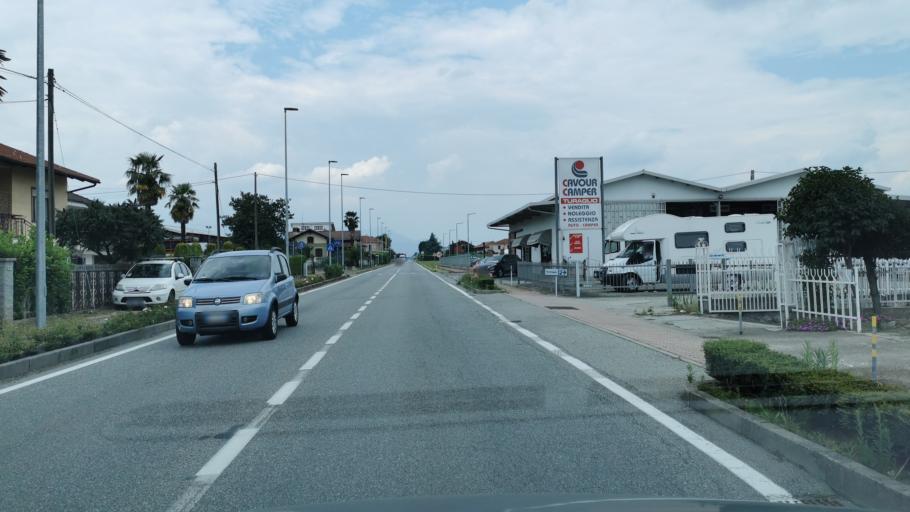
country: IT
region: Piedmont
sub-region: Provincia di Torino
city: Cavour
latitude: 44.7972
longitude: 7.3743
